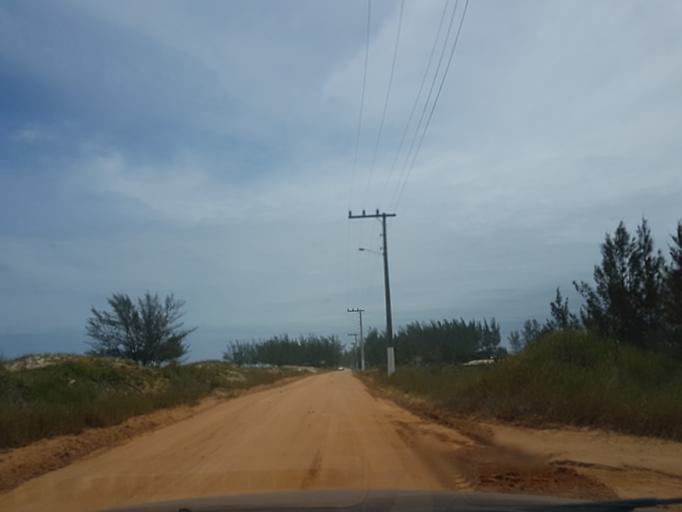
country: BR
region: Santa Catarina
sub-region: Jaguaruna
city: Jaguaruna
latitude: -28.6699
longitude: -48.9733
